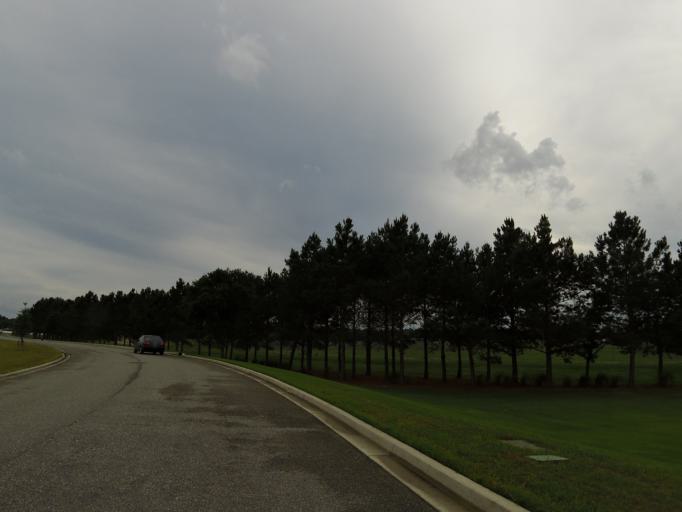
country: US
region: Florida
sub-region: Nassau County
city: Nassau Village-Ratliff
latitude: 30.5469
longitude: -81.7222
